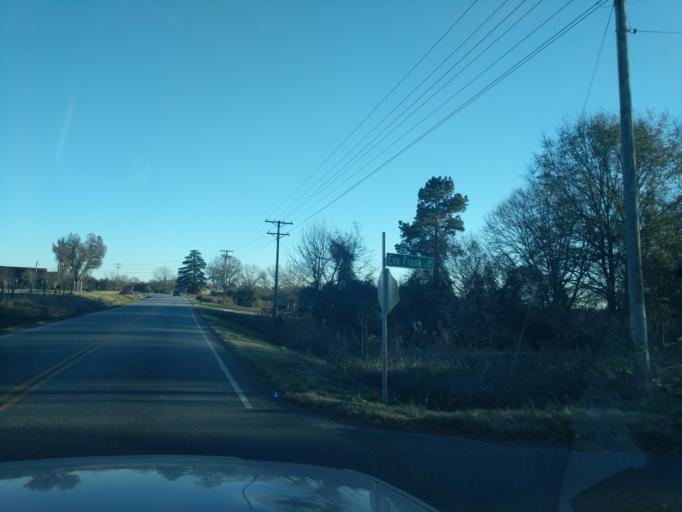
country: US
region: South Carolina
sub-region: Oconee County
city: Westminster
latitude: 34.6068
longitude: -83.0370
